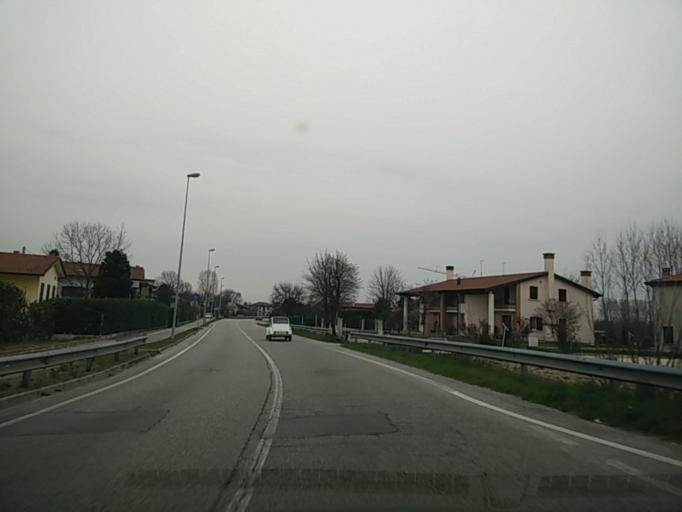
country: IT
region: Veneto
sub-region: Provincia di Venezia
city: Moniego
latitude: 45.5619
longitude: 12.0928
